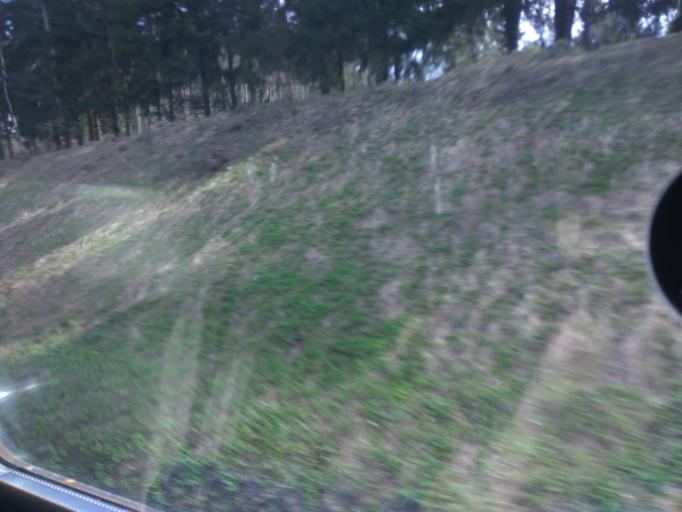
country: RU
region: Moskovskaya
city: Lugovaya
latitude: 56.0604
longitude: 37.4871
